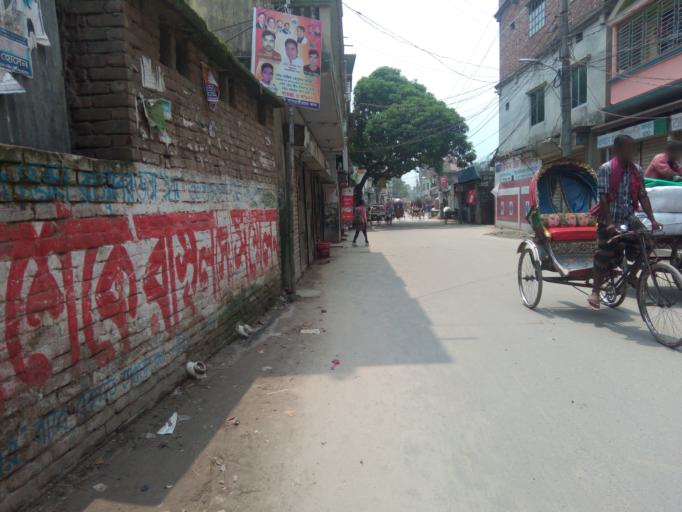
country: BD
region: Dhaka
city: Azimpur
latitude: 23.7169
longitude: 90.3704
